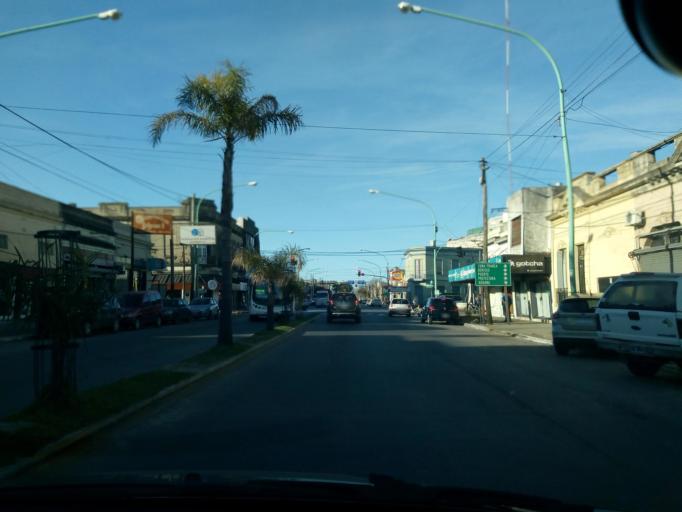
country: AR
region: Buenos Aires
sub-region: Partido de Ensenada
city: Ensenada
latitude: -34.8630
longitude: -57.9025
